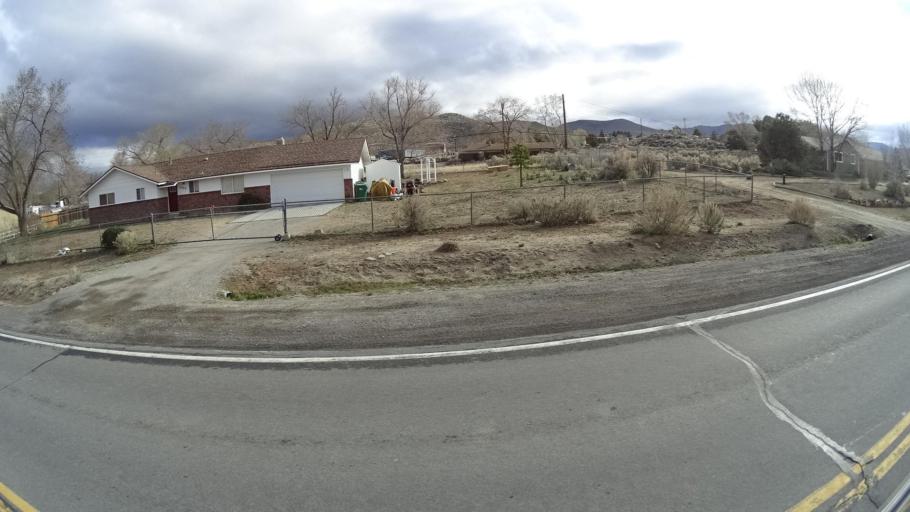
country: US
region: Nevada
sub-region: Storey County
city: Virginia City
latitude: 39.3012
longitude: -119.7818
